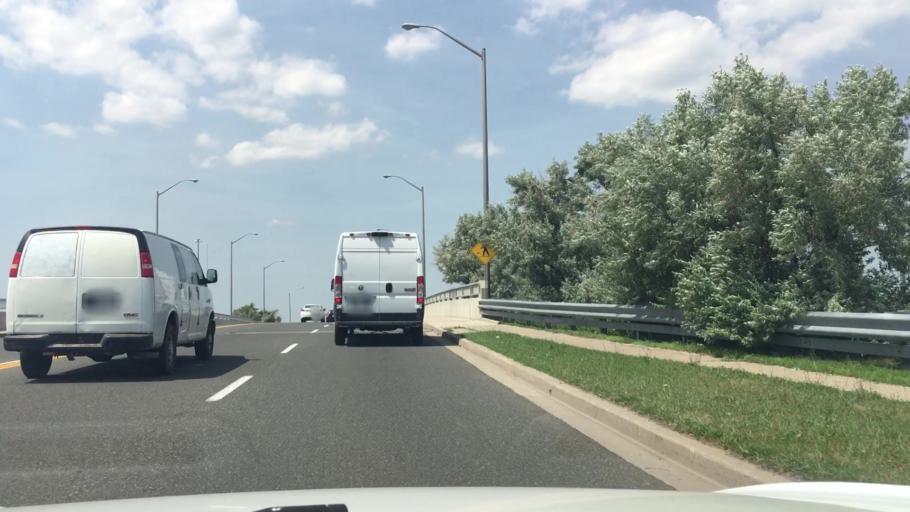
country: CA
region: Ontario
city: Scarborough
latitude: 43.7699
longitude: -79.2931
